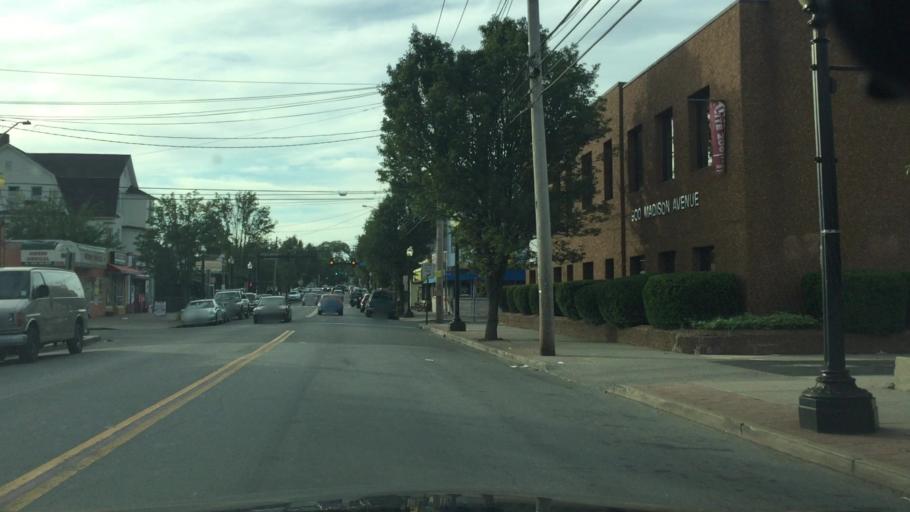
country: US
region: Connecticut
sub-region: Fairfield County
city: Bridgeport
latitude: 41.1931
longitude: -73.2051
